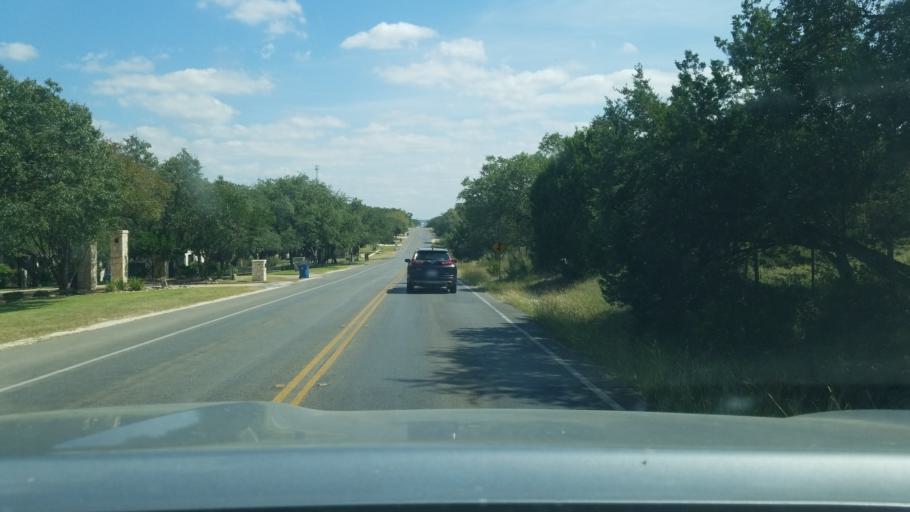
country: US
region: Texas
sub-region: Bexar County
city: Fair Oaks Ranch
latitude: 29.7311
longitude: -98.6325
